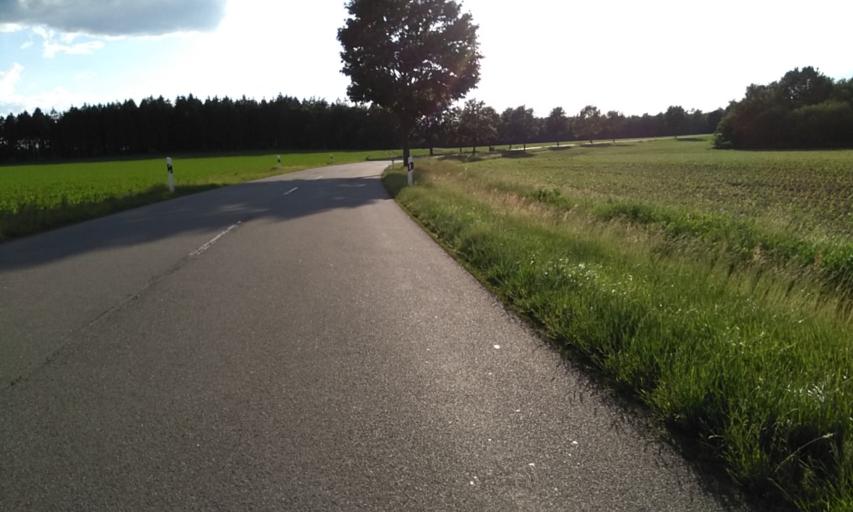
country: DE
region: Lower Saxony
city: Heeslingen
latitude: 53.3520
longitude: 9.3491
